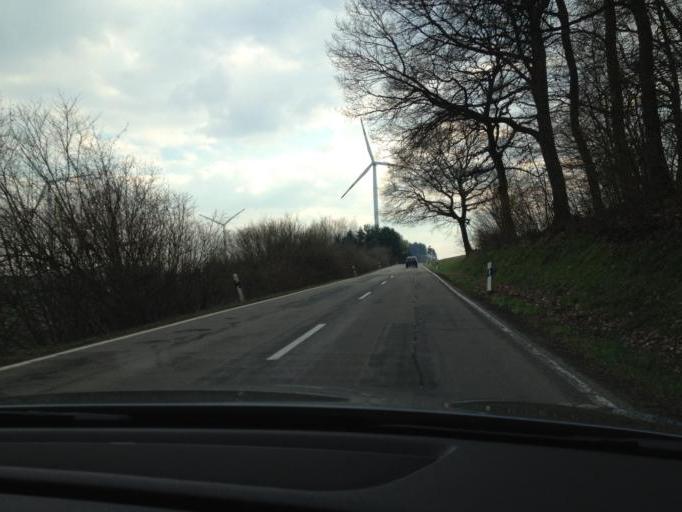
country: DE
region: Saarland
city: Freisen
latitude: 49.5138
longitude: 7.2470
